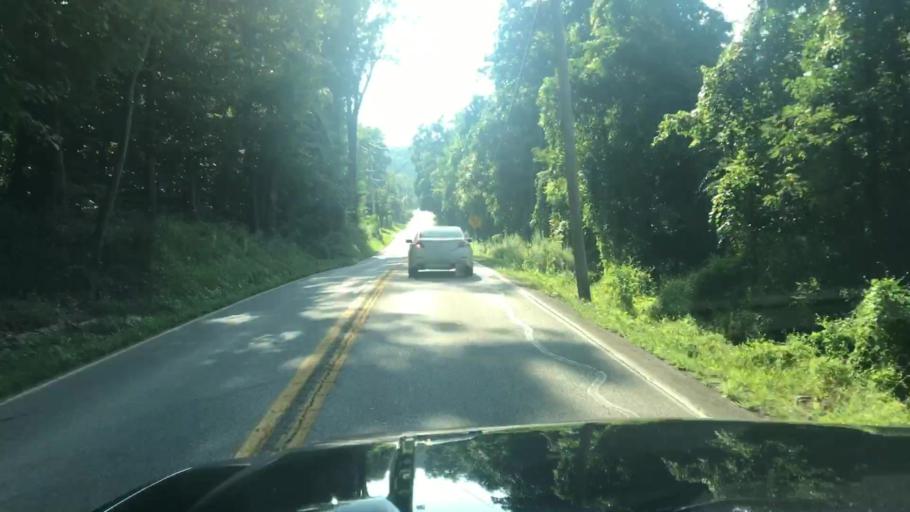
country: US
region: Pennsylvania
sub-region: York County
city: Valley Green
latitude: 40.1507
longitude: -76.8268
